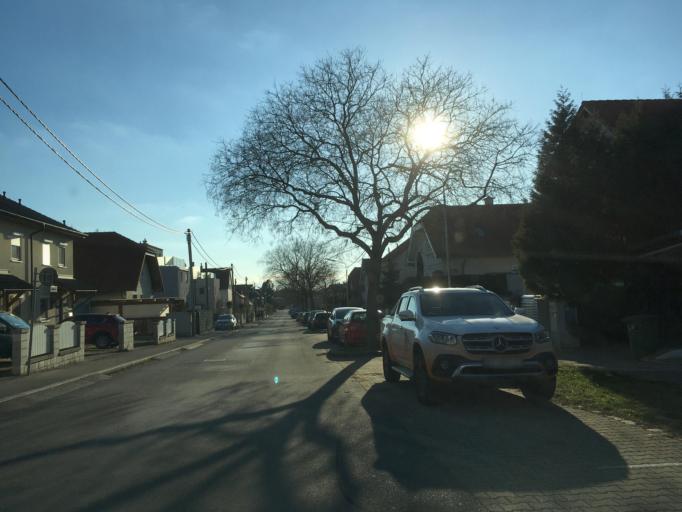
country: AT
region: Lower Austria
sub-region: Politischer Bezirk Wien-Umgebung
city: Leopoldsdorf
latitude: 48.1424
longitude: 16.3965
